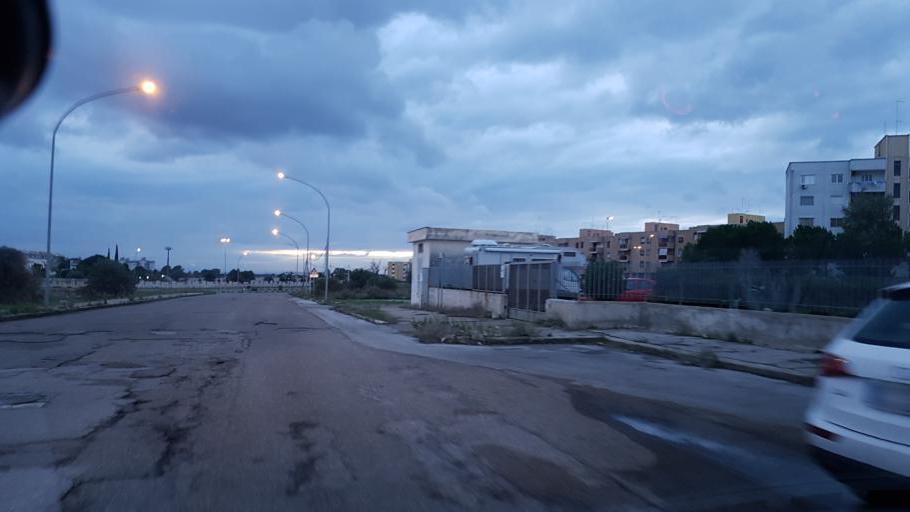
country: IT
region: Apulia
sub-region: Provincia di Taranto
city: Paolo VI
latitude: 40.5313
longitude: 17.2836
